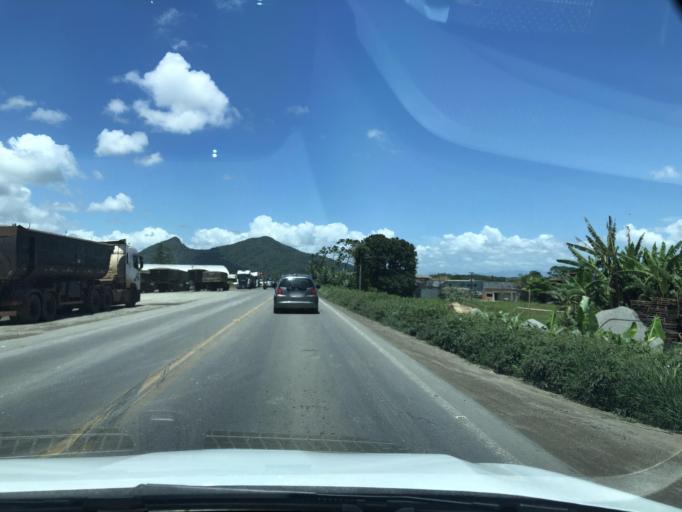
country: BR
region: Santa Catarina
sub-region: Sao Francisco Do Sul
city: Sao Francisco do Sul
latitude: -26.2678
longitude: -48.6368
